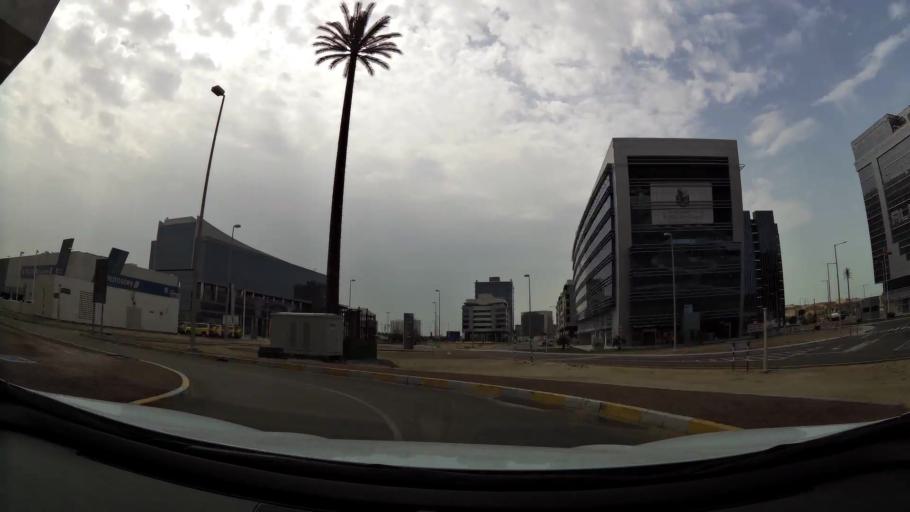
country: AE
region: Abu Dhabi
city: Abu Dhabi
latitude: 24.4308
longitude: 54.4653
